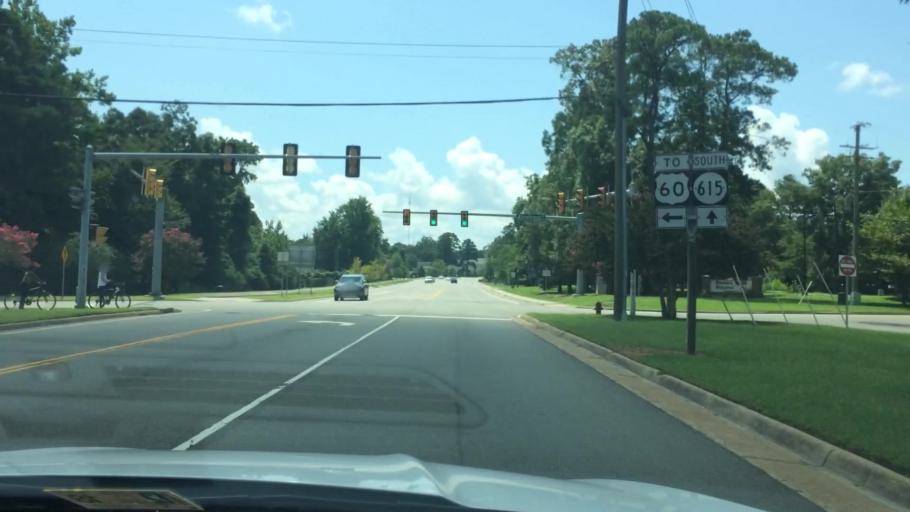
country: US
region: Virginia
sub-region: James City County
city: Williamsburg
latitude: 37.2897
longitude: -76.7339
